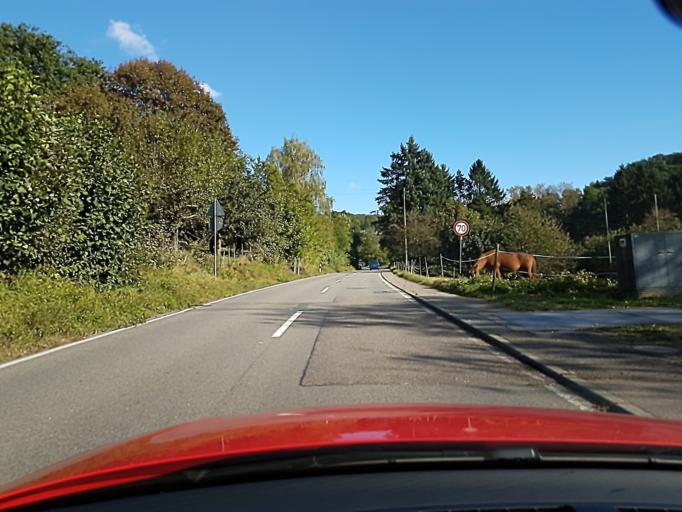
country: DE
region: Hesse
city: Neckarsteinach
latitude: 49.3961
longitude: 8.8328
